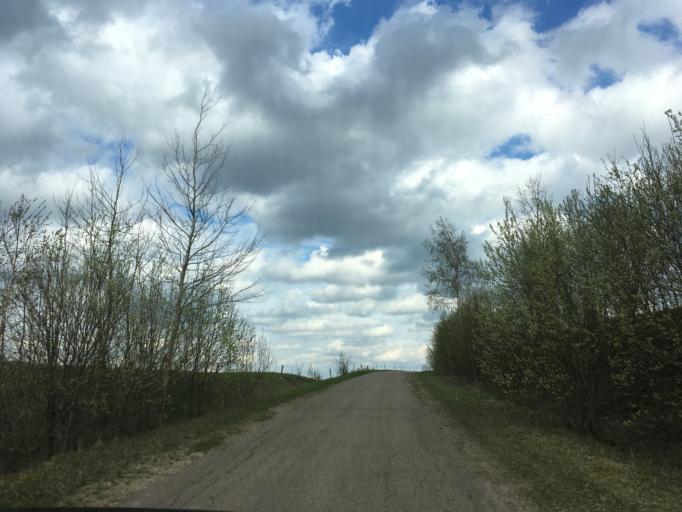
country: PL
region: Podlasie
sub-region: Suwalki
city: Suwalki
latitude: 54.3700
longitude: 22.8916
